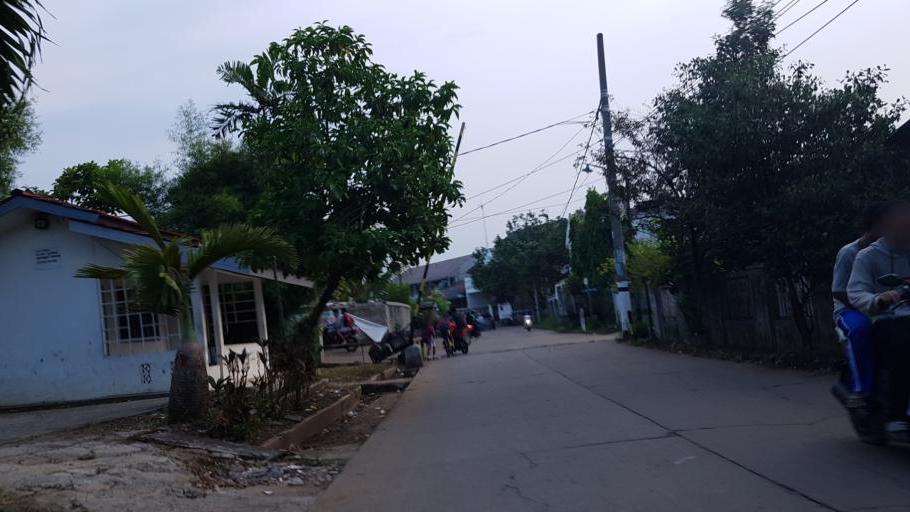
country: ID
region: West Java
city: Bekasi
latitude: -6.2699
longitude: 106.9469
